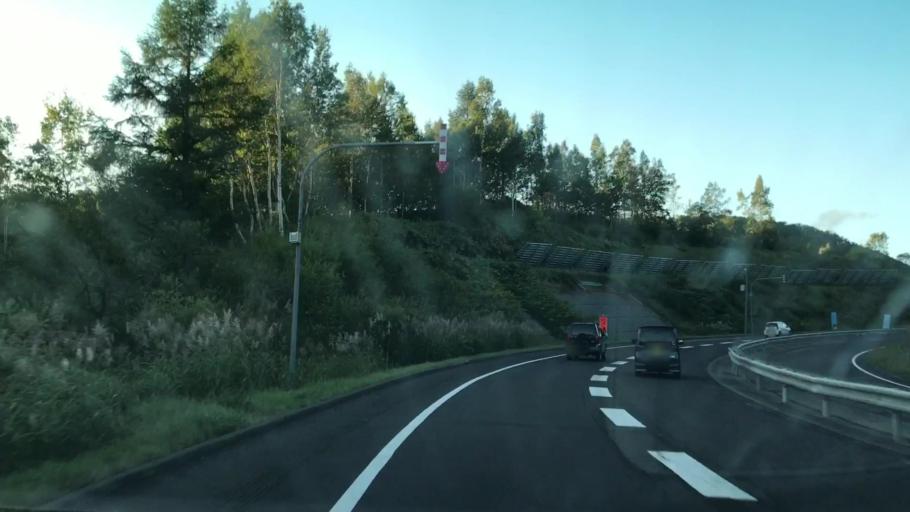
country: JP
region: Hokkaido
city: Otaru
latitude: 42.8479
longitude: 141.0668
